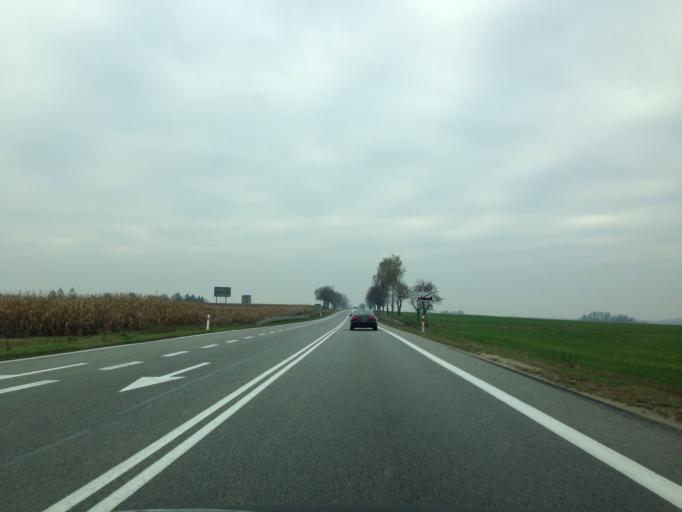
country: PL
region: Masovian Voivodeship
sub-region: Powiat plonski
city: Dzierzaznia
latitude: 52.6382
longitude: 20.1439
